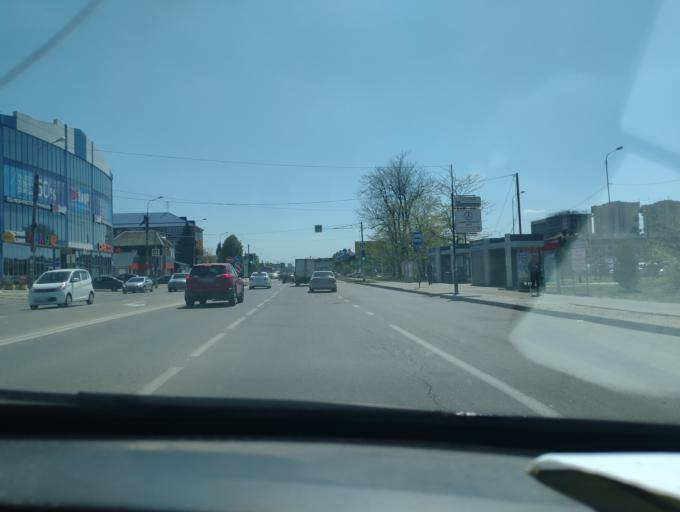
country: RU
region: Krasnodarskiy
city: Krasnodar
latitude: 45.0877
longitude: 39.0142
